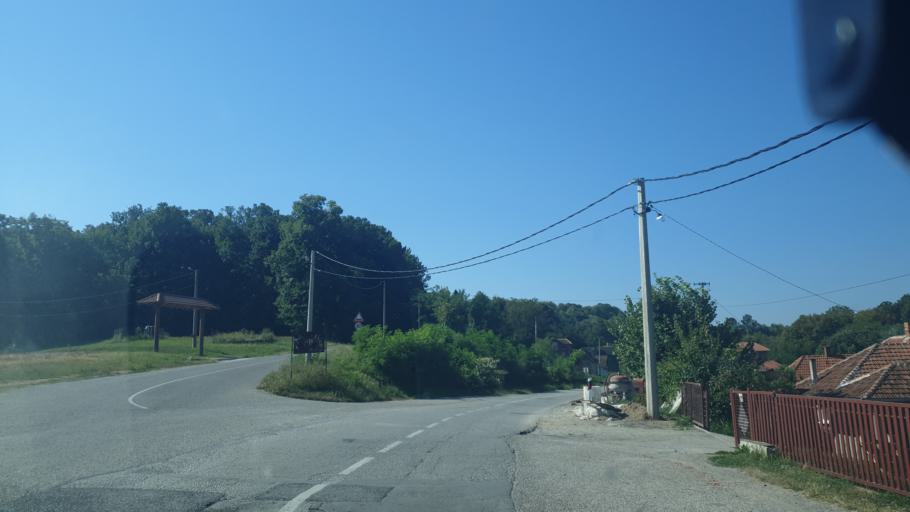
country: RS
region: Central Serbia
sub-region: Kolubarski Okrug
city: Lajkovac
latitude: 44.3070
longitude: 20.1523
